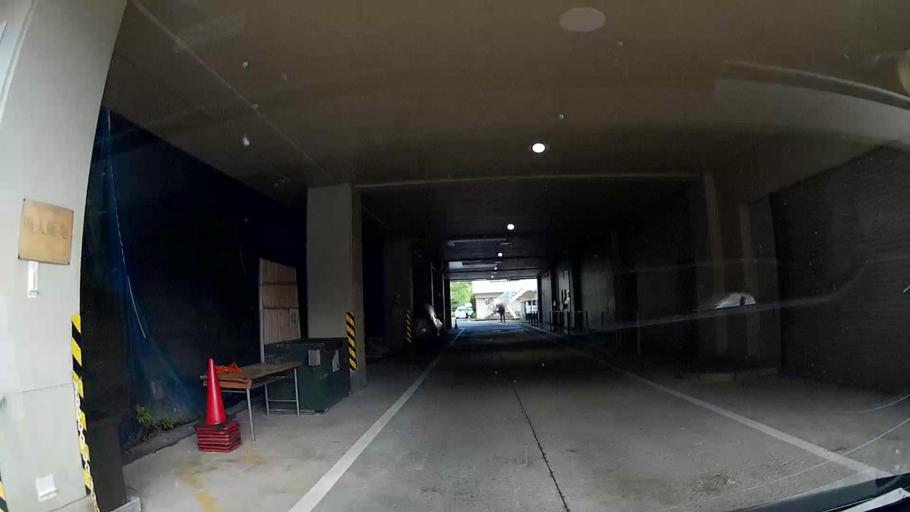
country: JP
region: Shizuoka
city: Shizuoka-shi
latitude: 35.2112
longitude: 138.2233
